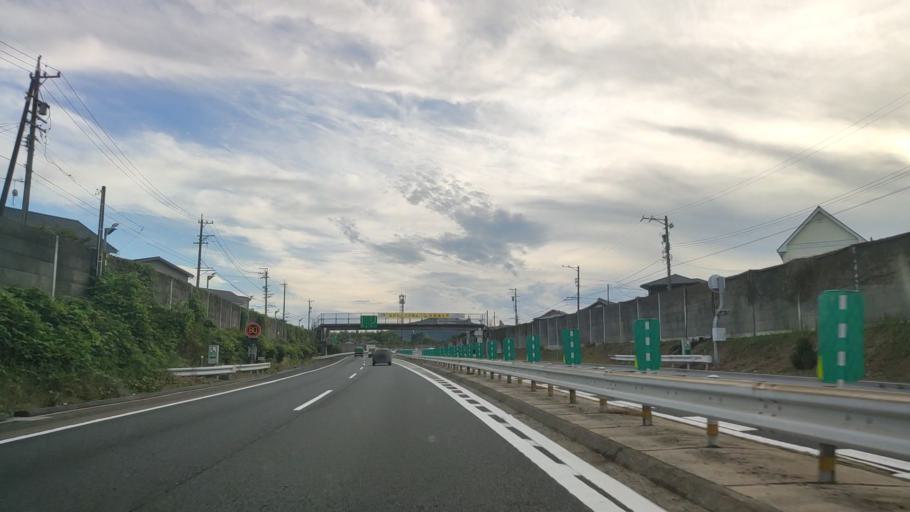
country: JP
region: Gifu
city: Tajimi
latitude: 35.3457
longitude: 137.1019
